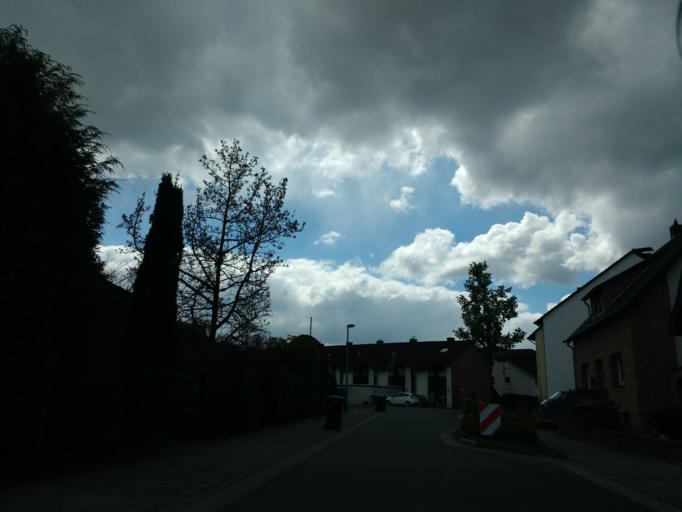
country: DE
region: North Rhine-Westphalia
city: Bad Lippspringe
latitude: 51.7894
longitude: 8.8243
